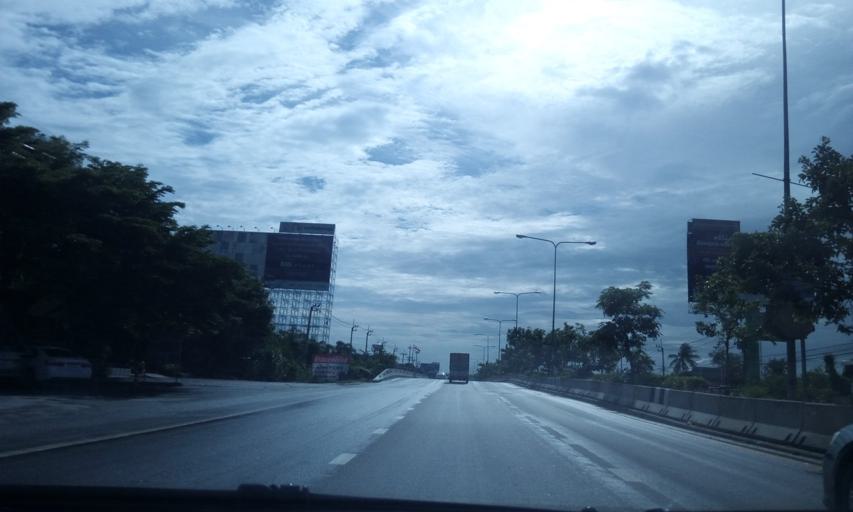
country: TH
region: Nonthaburi
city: Pak Kret
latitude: 13.9240
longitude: 100.4719
